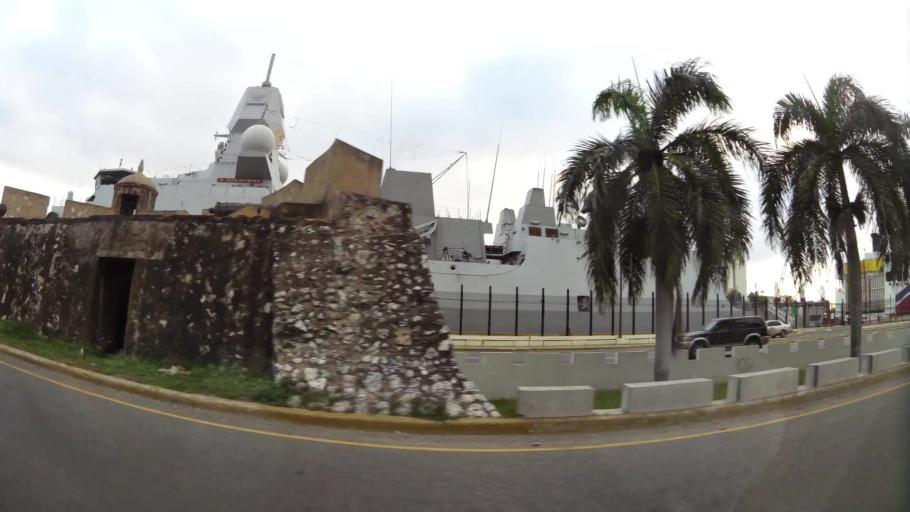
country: DO
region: Nacional
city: San Carlos
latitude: 18.4770
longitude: -69.8822
